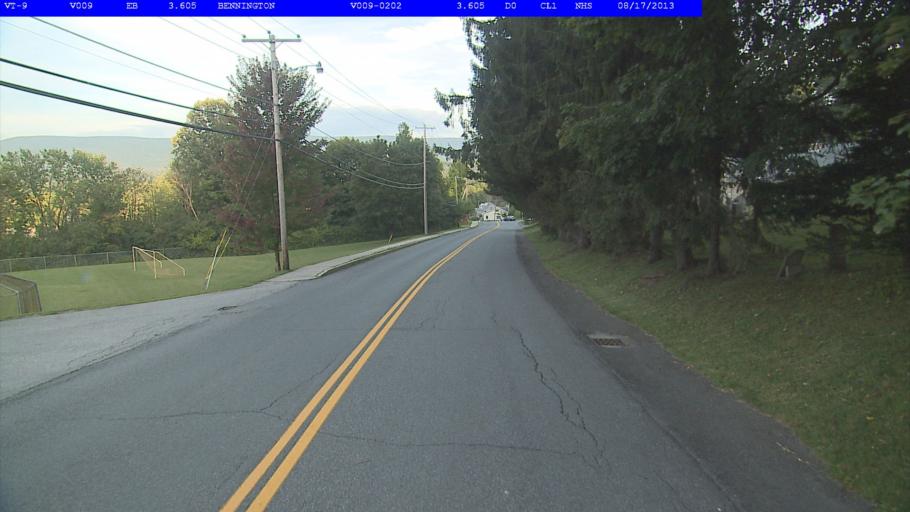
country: US
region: Vermont
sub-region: Bennington County
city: Bennington
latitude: 42.8840
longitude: -73.2105
